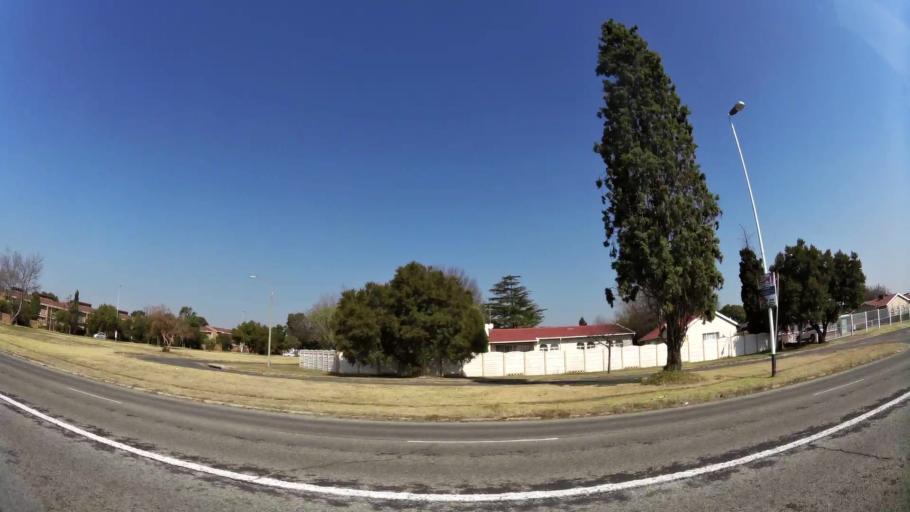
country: ZA
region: Gauteng
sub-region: Ekurhuleni Metropolitan Municipality
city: Boksburg
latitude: -26.2410
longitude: 28.2636
